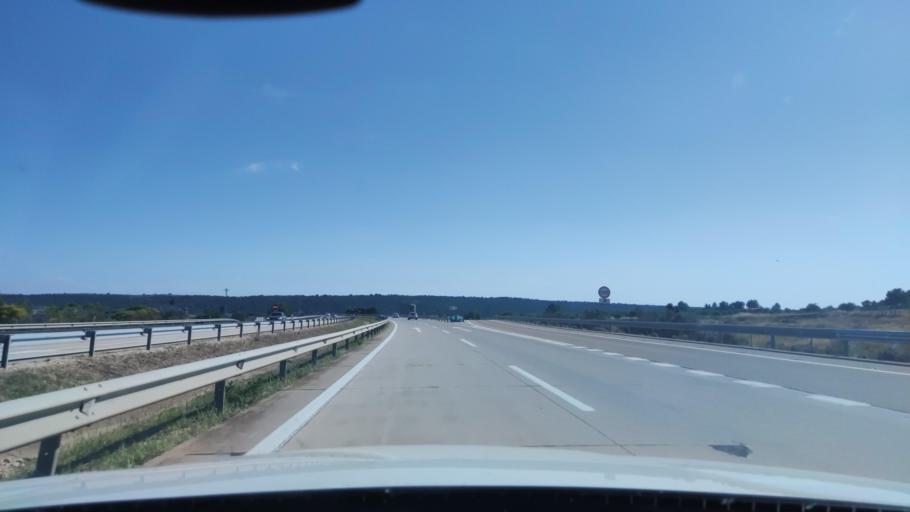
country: ES
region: Castille-La Mancha
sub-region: Provincia de Cuenca
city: Sisante
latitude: 39.4128
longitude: -2.2141
